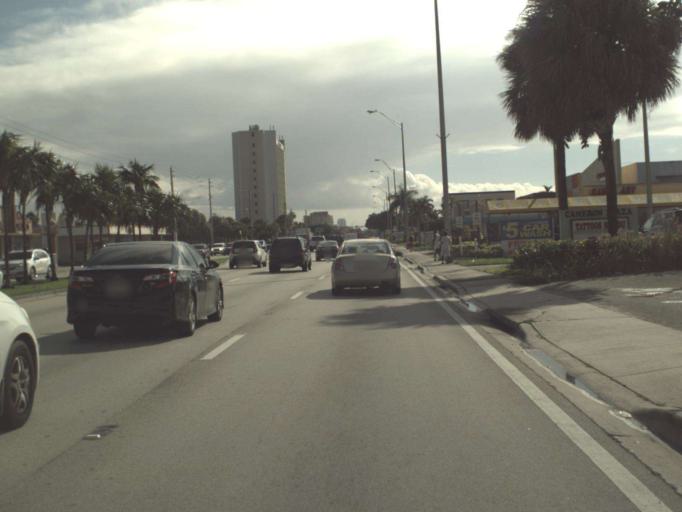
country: US
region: Florida
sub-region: Miami-Dade County
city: Golden Glades
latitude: 25.9283
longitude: -80.1917
